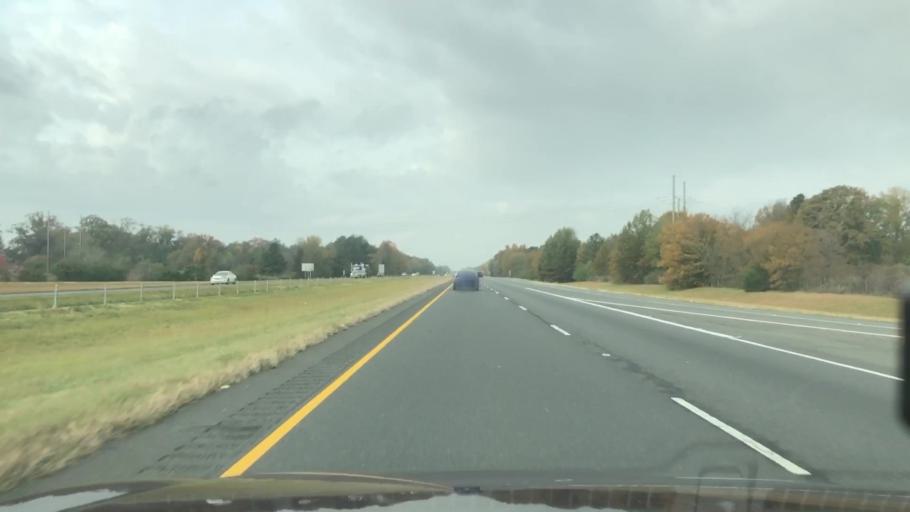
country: US
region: Louisiana
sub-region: Richland Parish
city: Delhi
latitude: 32.4517
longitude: -91.5842
